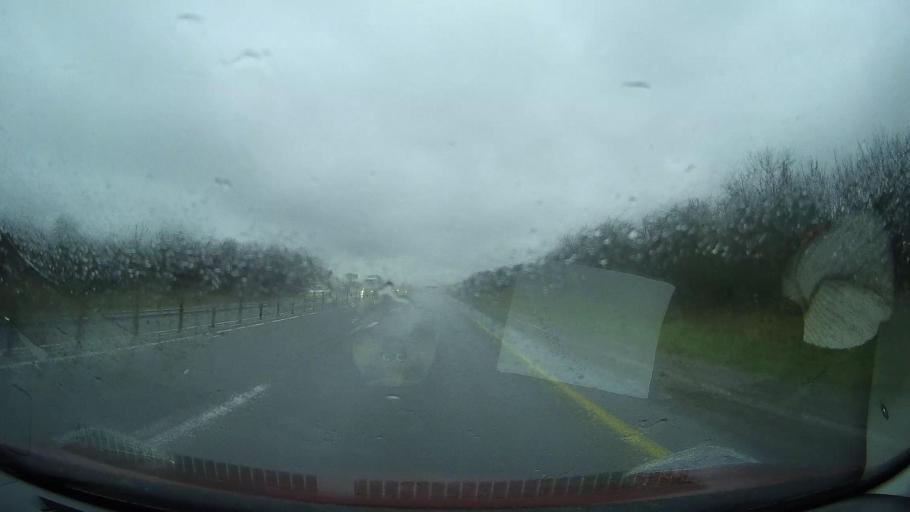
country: RU
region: Stavropol'skiy
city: Nevinnomyssk
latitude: 44.6391
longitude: 41.9781
